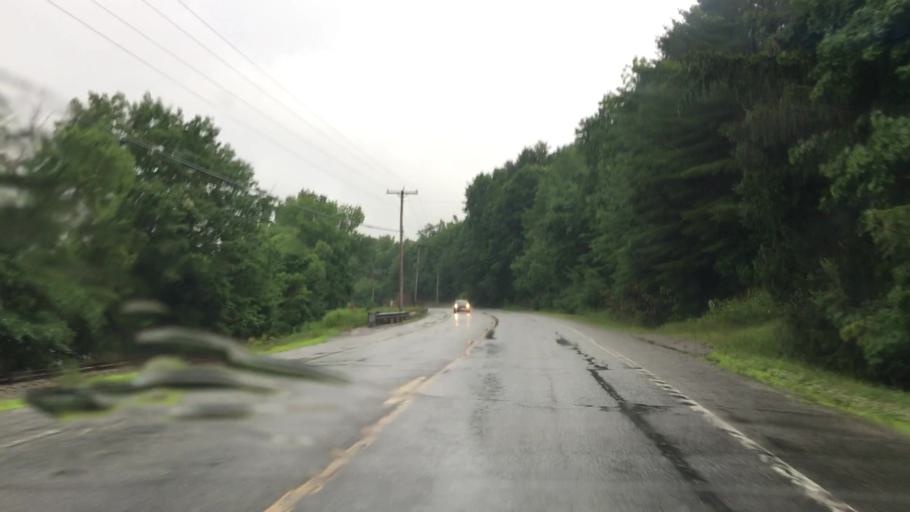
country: US
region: Maine
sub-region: Kennebec County
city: Pittston
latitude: 44.2072
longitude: -69.7648
